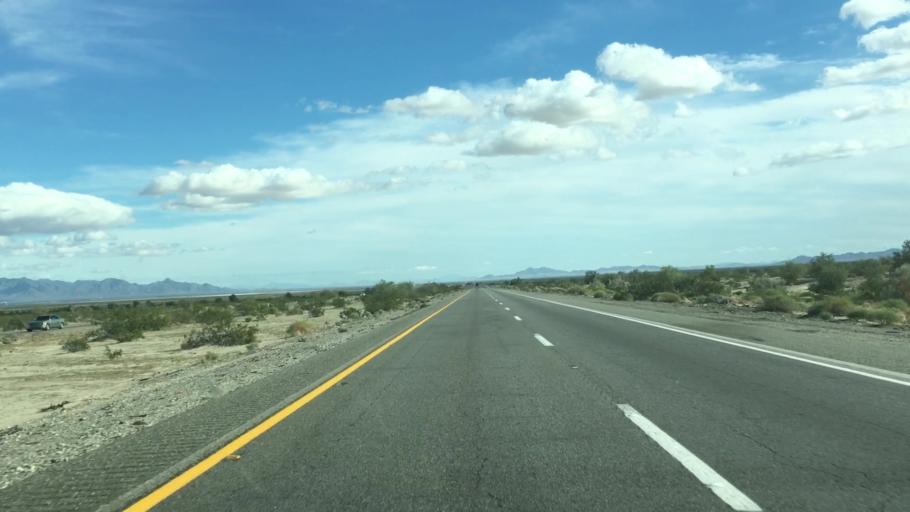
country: US
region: California
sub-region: Riverside County
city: Mesa Verde
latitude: 33.6537
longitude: -115.1467
